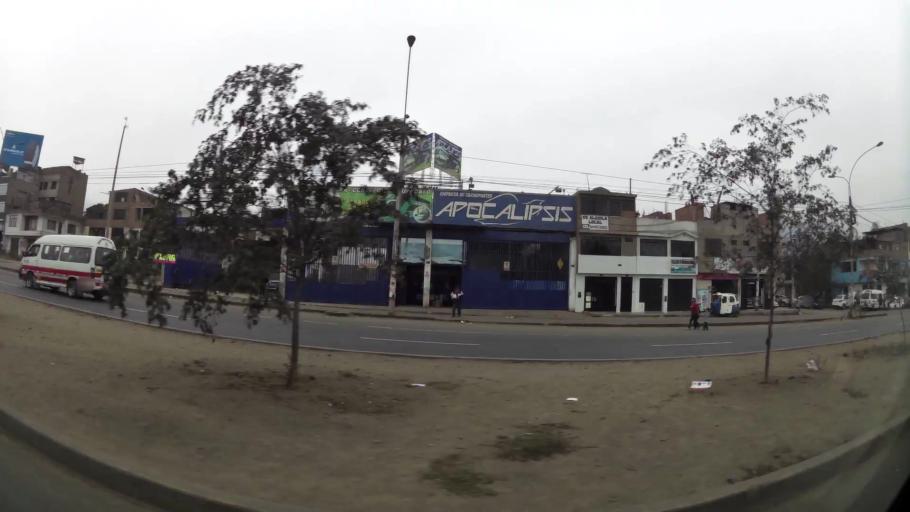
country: PE
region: Lima
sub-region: Lima
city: Urb. Santo Domingo
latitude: -11.9189
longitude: -77.0417
